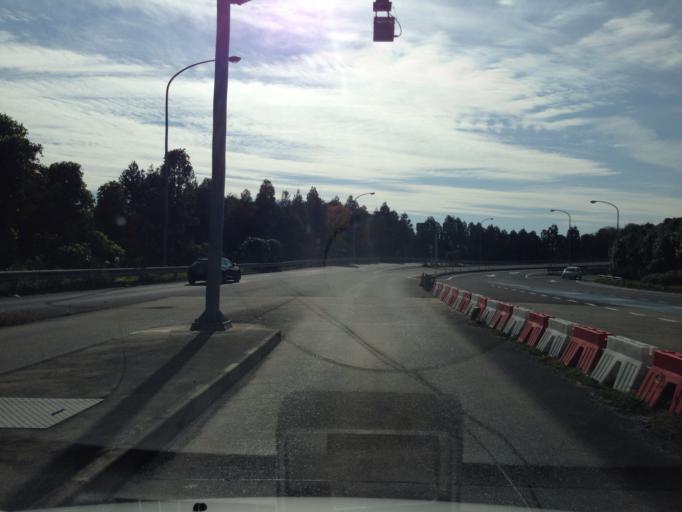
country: JP
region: Ibaraki
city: Naka
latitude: 36.0580
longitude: 140.1577
